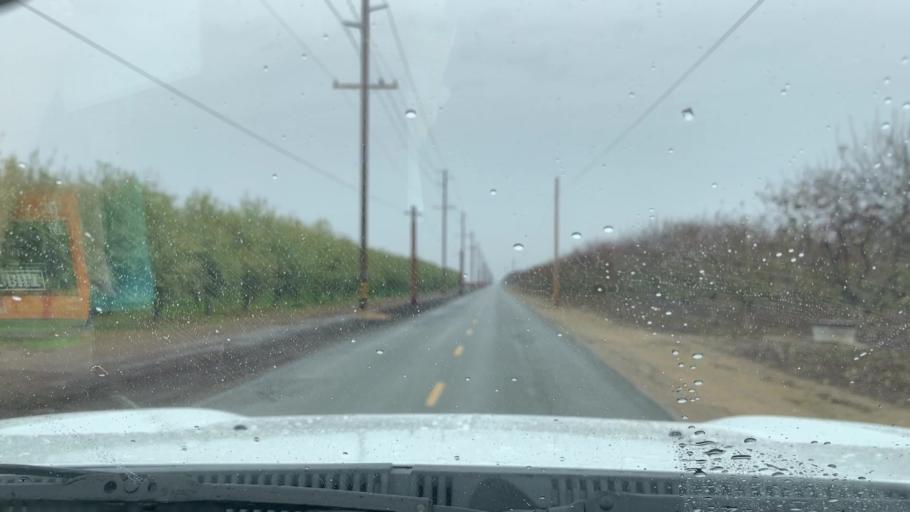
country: US
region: California
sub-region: Kern County
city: Delano
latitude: 35.8341
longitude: -119.1915
